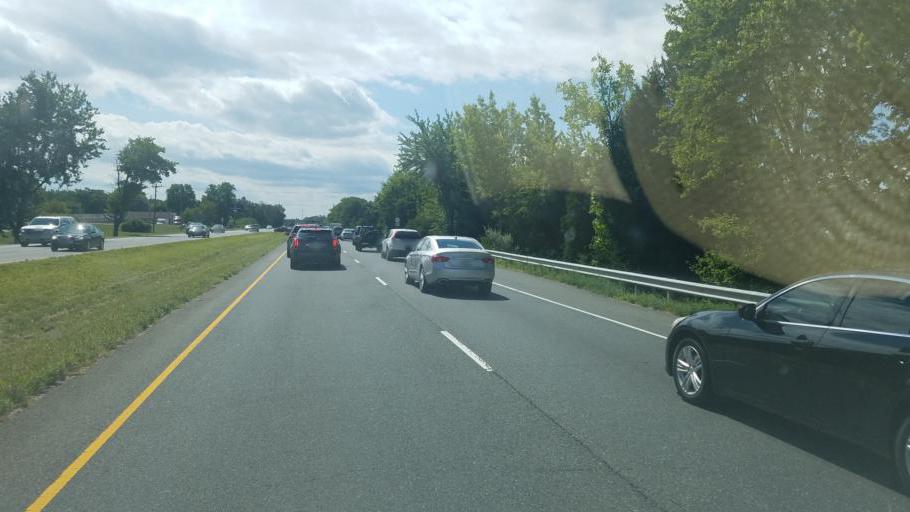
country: US
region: Virginia
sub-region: Stafford County
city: Falmouth
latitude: 38.3773
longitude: -77.5357
